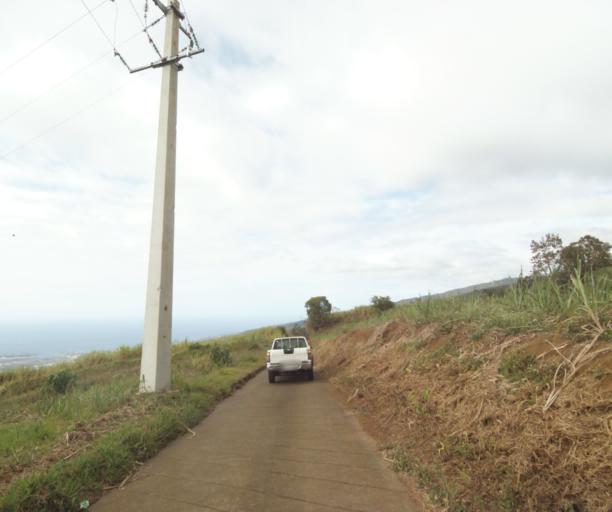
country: RE
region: Reunion
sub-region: Reunion
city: Saint-Paul
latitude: -21.0081
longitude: 55.3486
